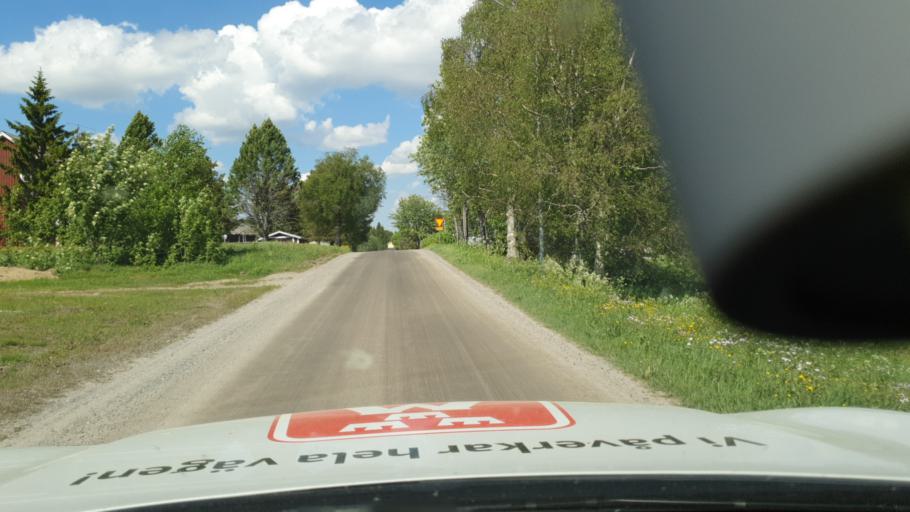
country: SE
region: Vaesterbotten
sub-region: Robertsfors Kommun
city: Robertsfors
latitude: 64.2270
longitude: 21.0199
